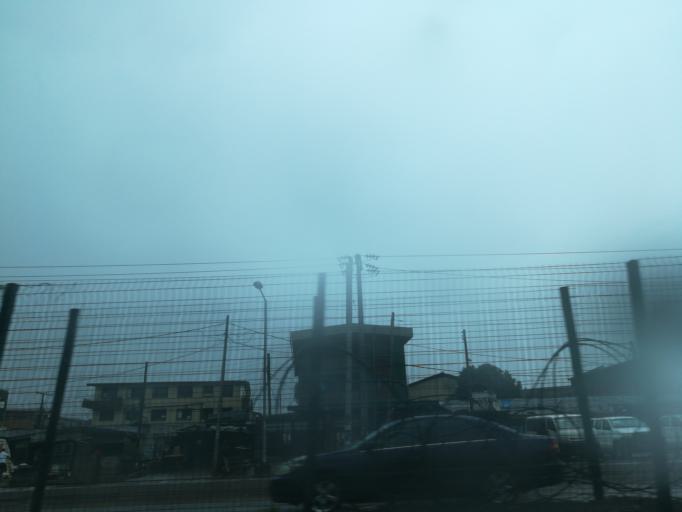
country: NG
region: Lagos
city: Ojota
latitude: 6.6023
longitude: 3.3895
